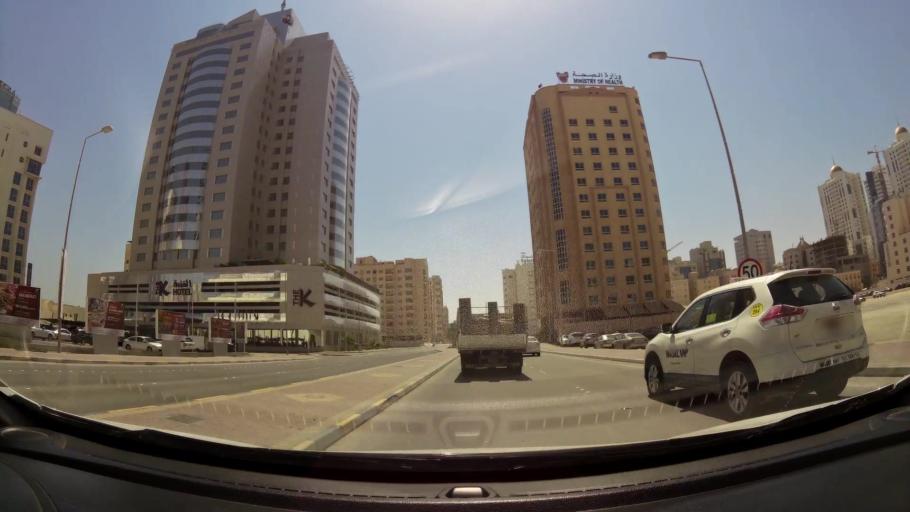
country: BH
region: Manama
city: Manama
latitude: 26.2148
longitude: 50.6099
